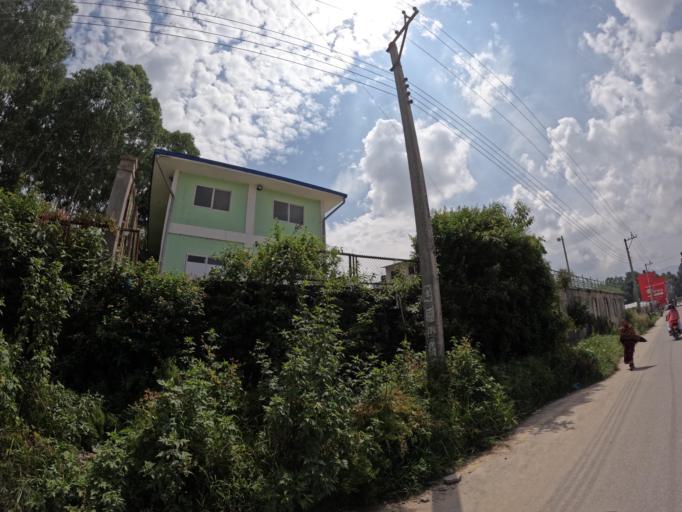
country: NP
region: Central Region
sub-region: Bagmati Zone
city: Bhaktapur
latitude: 27.6793
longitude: 85.3834
